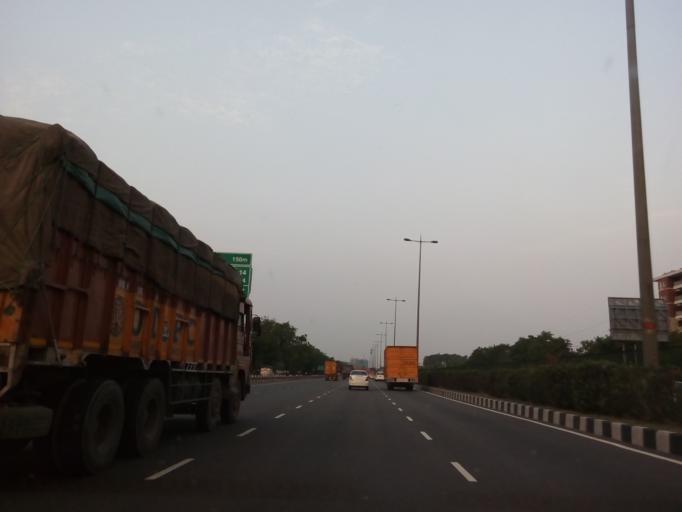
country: IN
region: Haryana
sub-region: Gurgaon
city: Gurgaon
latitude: 28.4726
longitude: 77.0624
